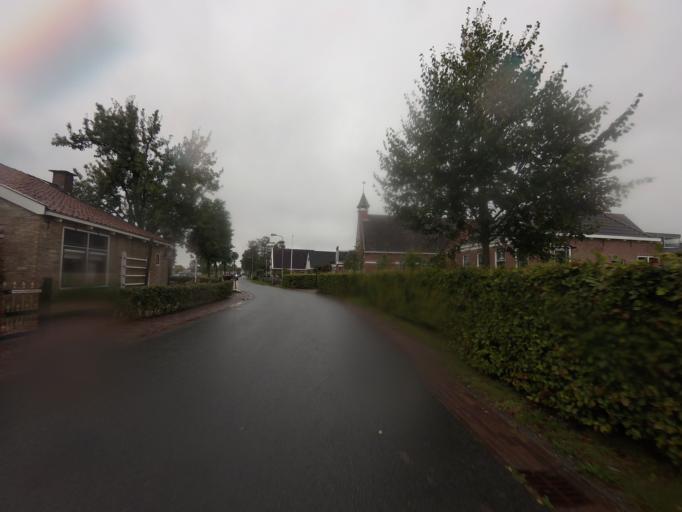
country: NL
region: Friesland
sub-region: Gemeente Tytsjerksteradiel
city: Garyp
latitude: 53.1315
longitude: 5.9416
